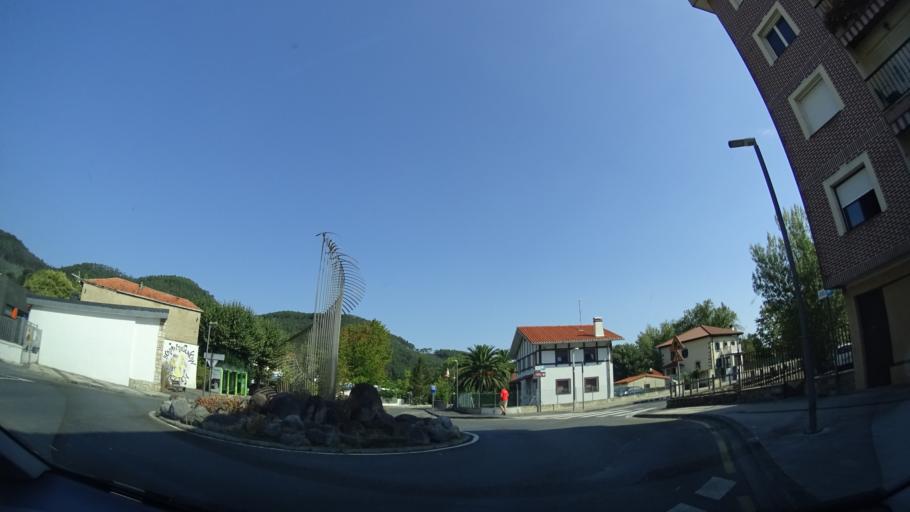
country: ES
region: Basque Country
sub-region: Bizkaia
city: Bakio
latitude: 43.4221
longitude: -2.8140
